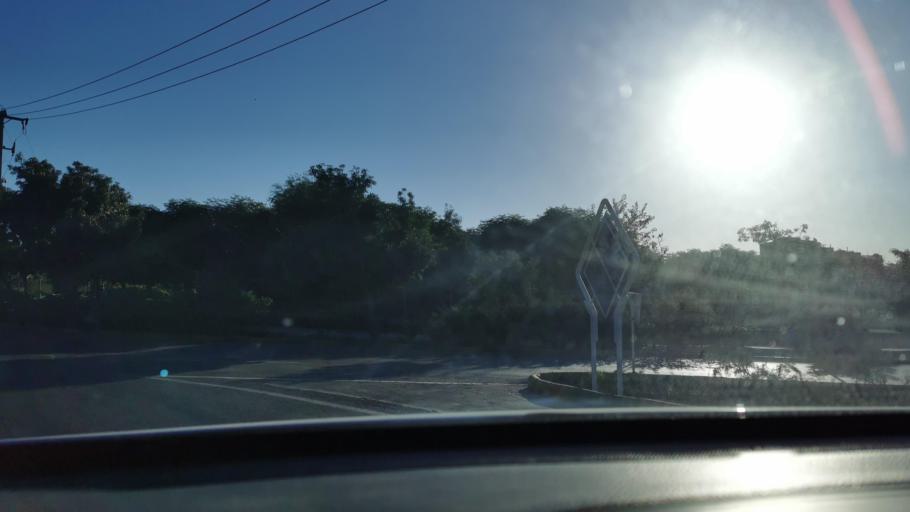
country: IR
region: Razavi Khorasan
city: Mashhad
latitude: 36.3471
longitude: 59.4771
